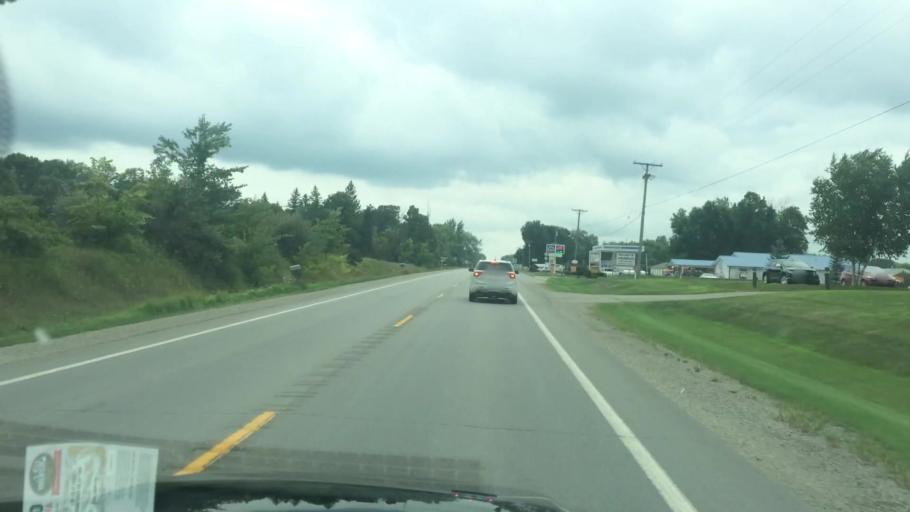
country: US
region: Michigan
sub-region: Tuscola County
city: Cass City
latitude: 43.5978
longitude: -83.0966
